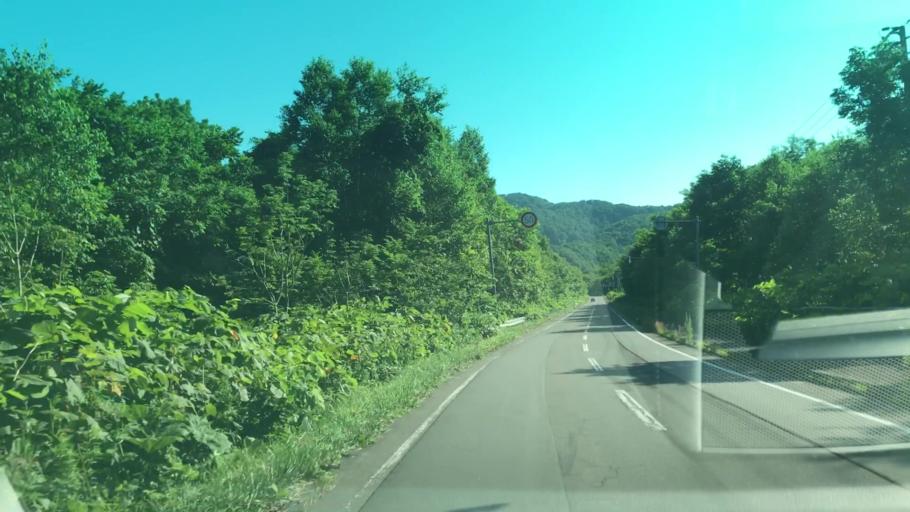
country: JP
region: Hokkaido
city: Yoichi
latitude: 43.0715
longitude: 140.7097
